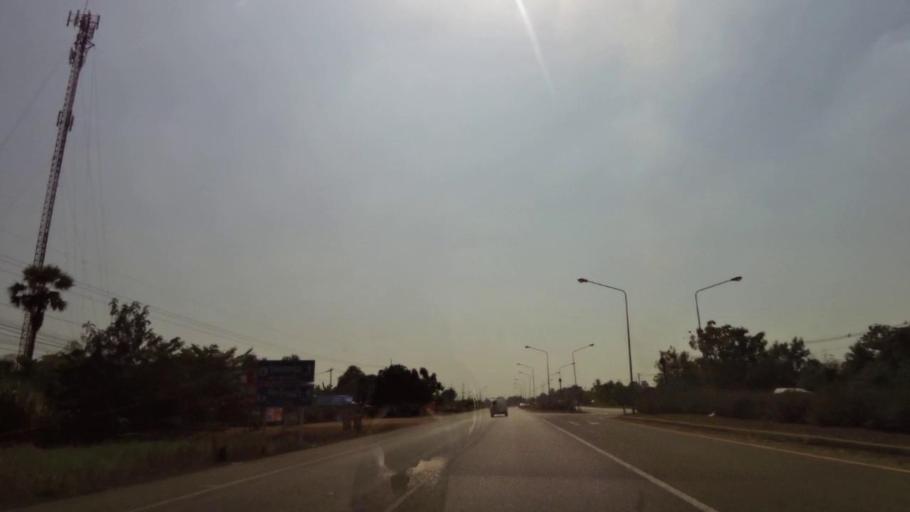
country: TH
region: Phichit
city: Wachira Barami
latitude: 16.3580
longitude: 100.1295
